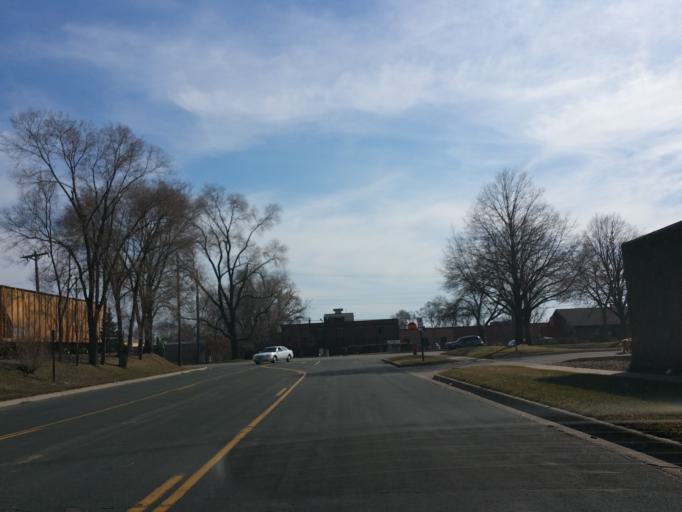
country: US
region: Minnesota
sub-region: Hennepin County
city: Bloomington
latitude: 44.8487
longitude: -93.2874
